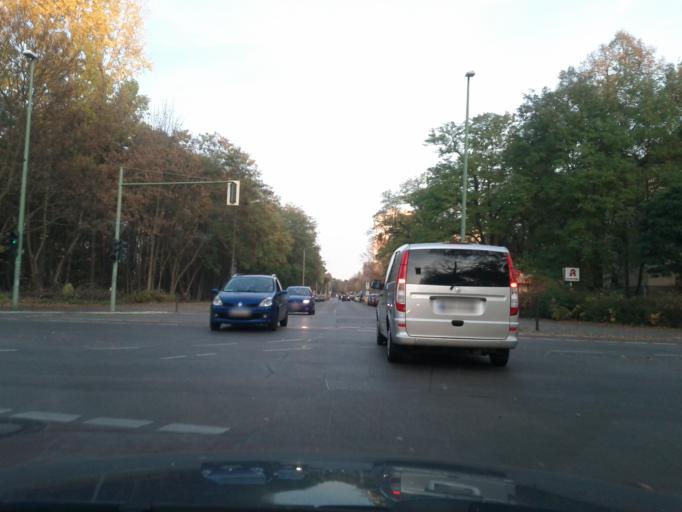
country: DE
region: Berlin
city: Berlin Koepenick
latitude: 52.4413
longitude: 13.5931
